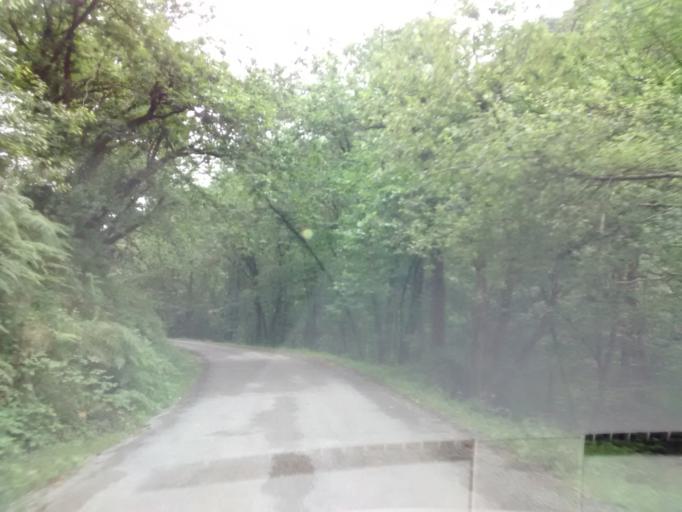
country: ES
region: Asturias
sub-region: Province of Asturias
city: Campo de Caso
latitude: 43.2682
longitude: -5.3394
